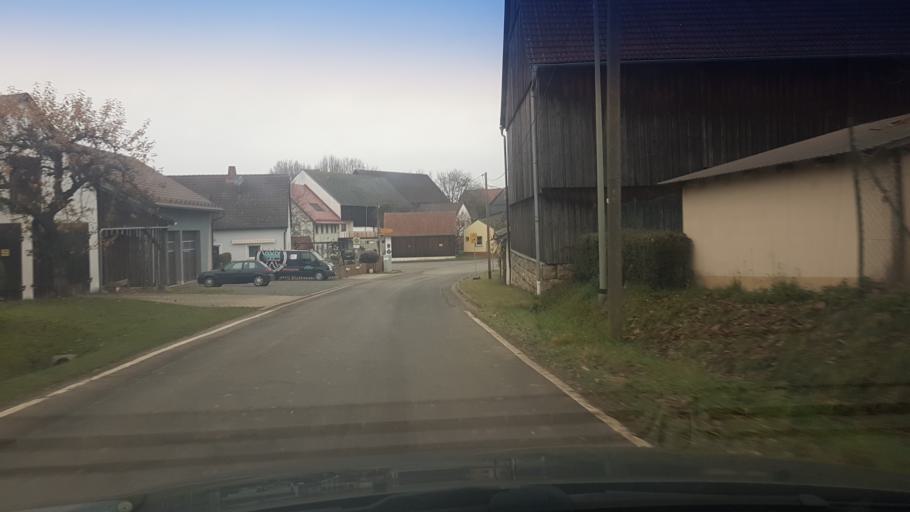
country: DE
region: Bavaria
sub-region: Upper Franconia
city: Stadelhofen
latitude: 50.0289
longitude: 11.2326
